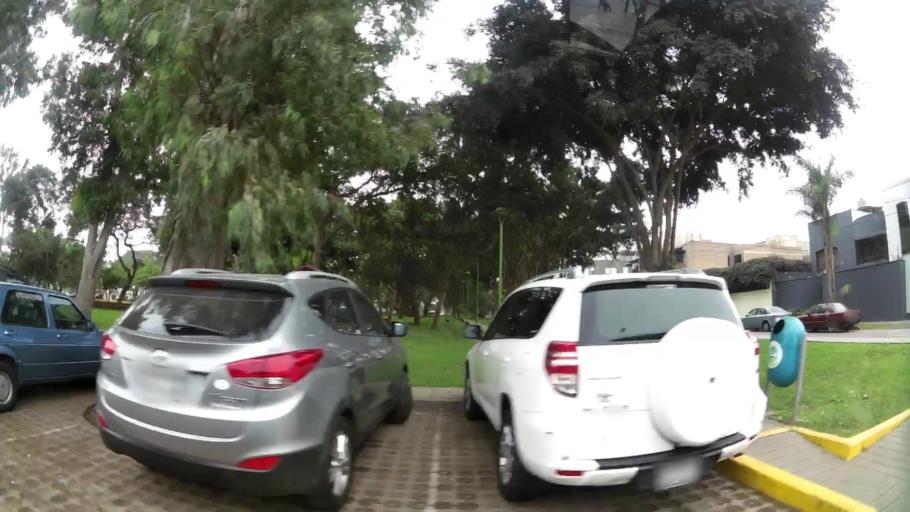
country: PE
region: Lima
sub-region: Lima
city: San Luis
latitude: -12.1078
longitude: -76.9827
